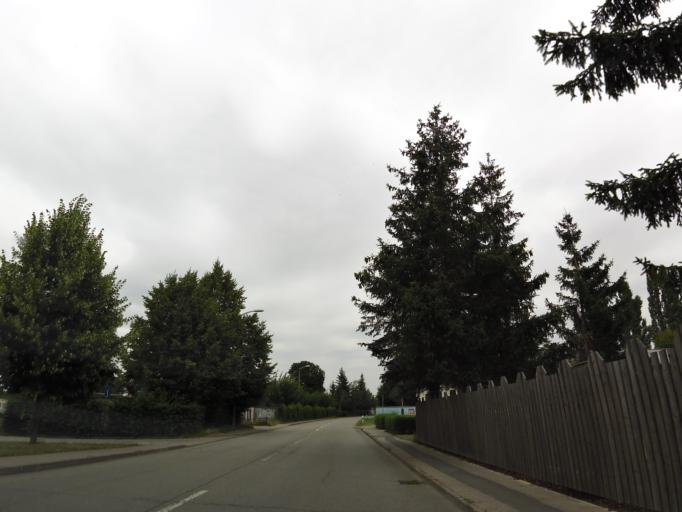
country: DE
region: Thuringia
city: Bad Langensalza
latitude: 51.1162
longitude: 10.6521
